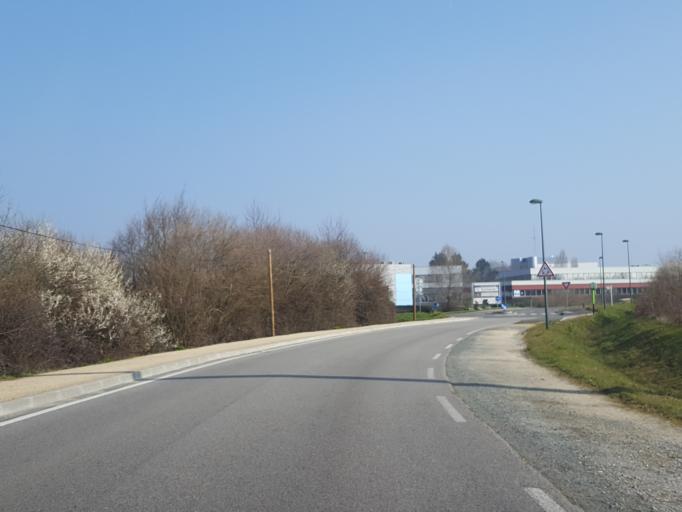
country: FR
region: Pays de la Loire
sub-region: Departement de la Vendee
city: La Roche-sur-Yon
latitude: 46.6808
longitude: -1.4526
